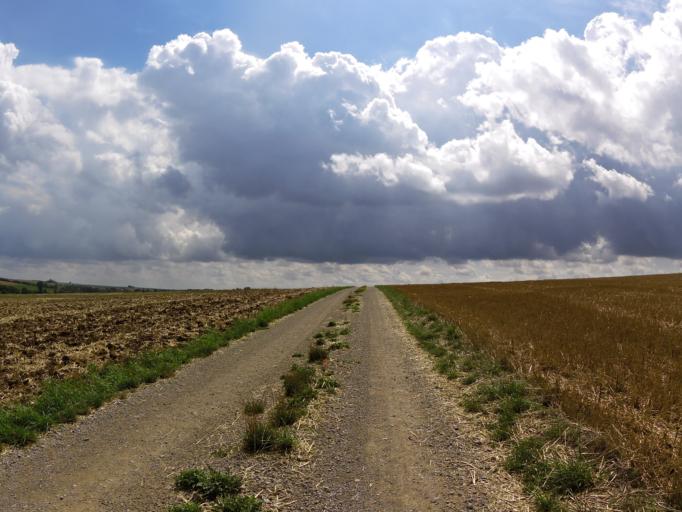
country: DE
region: Bavaria
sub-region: Regierungsbezirk Unterfranken
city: Reichenberg
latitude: 49.7202
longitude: 9.9115
